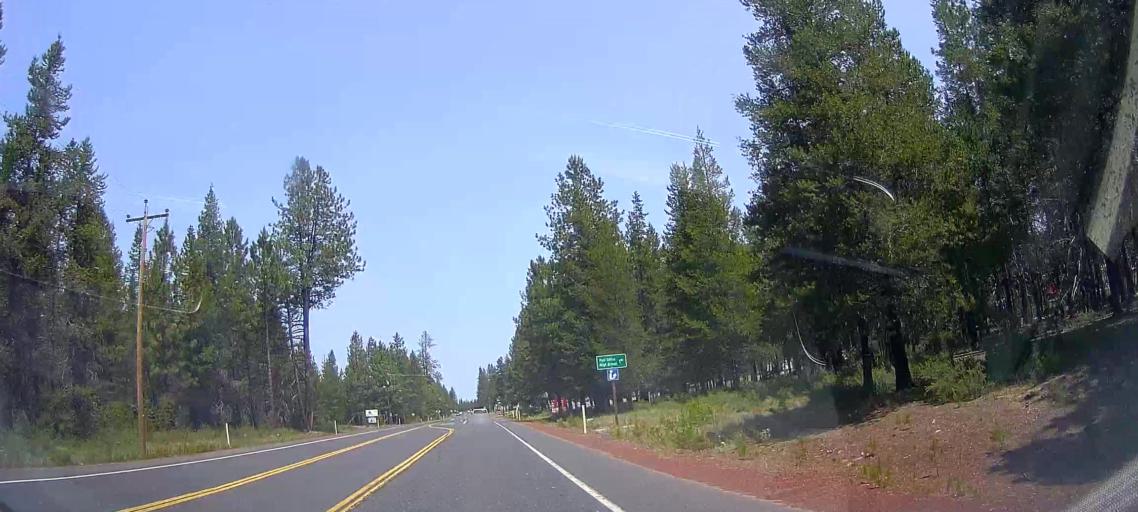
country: US
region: Oregon
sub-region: Deschutes County
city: La Pine
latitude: 43.4759
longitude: -121.6884
